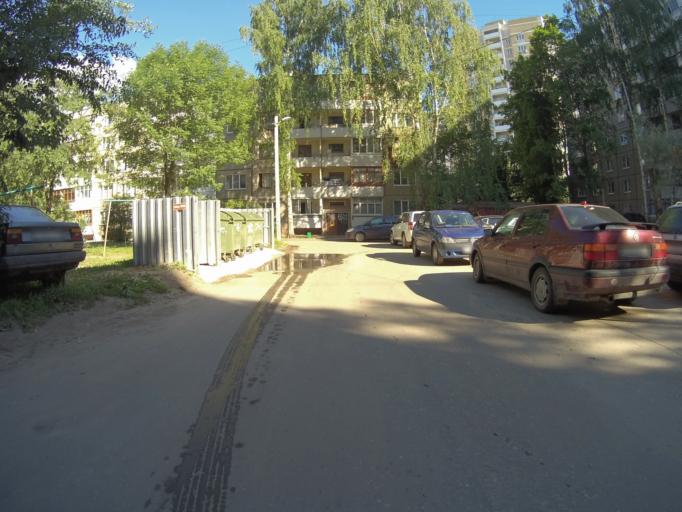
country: RU
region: Vladimir
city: Kommunar
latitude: 56.1628
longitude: 40.4674
